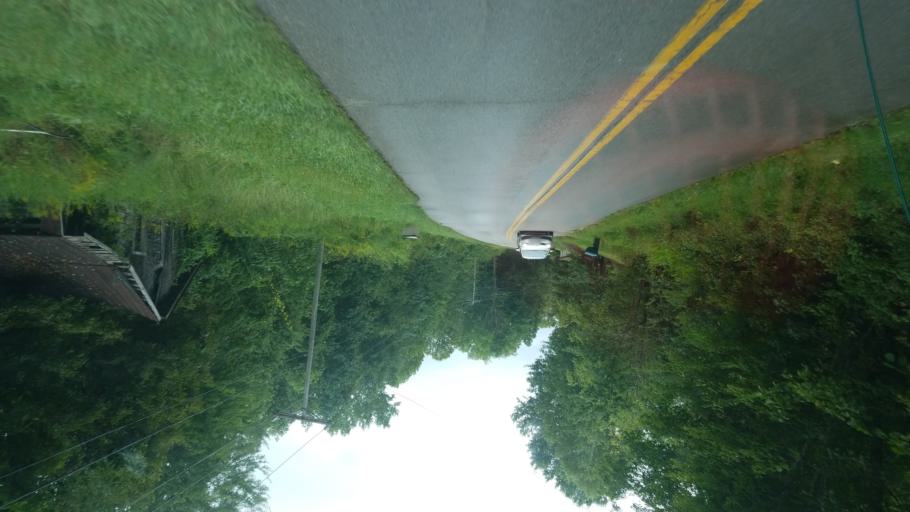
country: US
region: Kentucky
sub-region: Rowan County
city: Morehead
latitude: 38.3150
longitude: -83.5539
